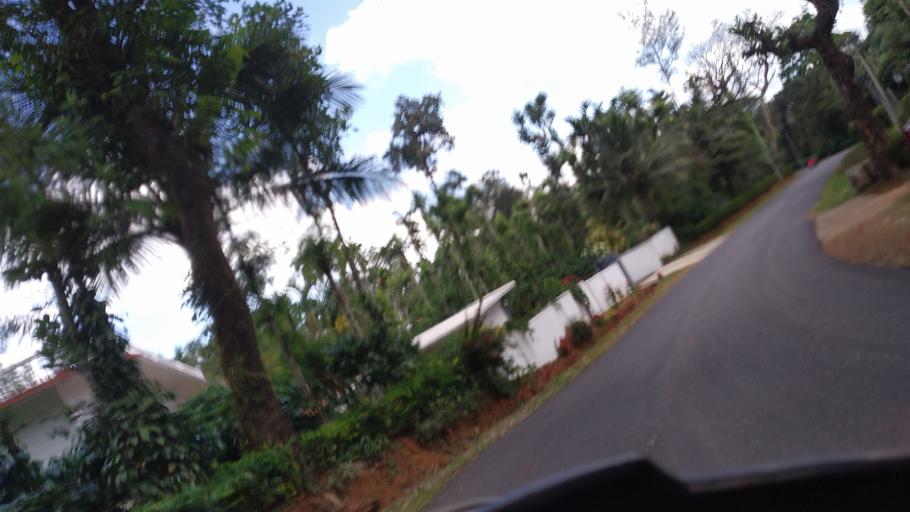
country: IN
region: Karnataka
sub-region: Kodagu
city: Ponnampet
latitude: 12.0339
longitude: 75.9271
